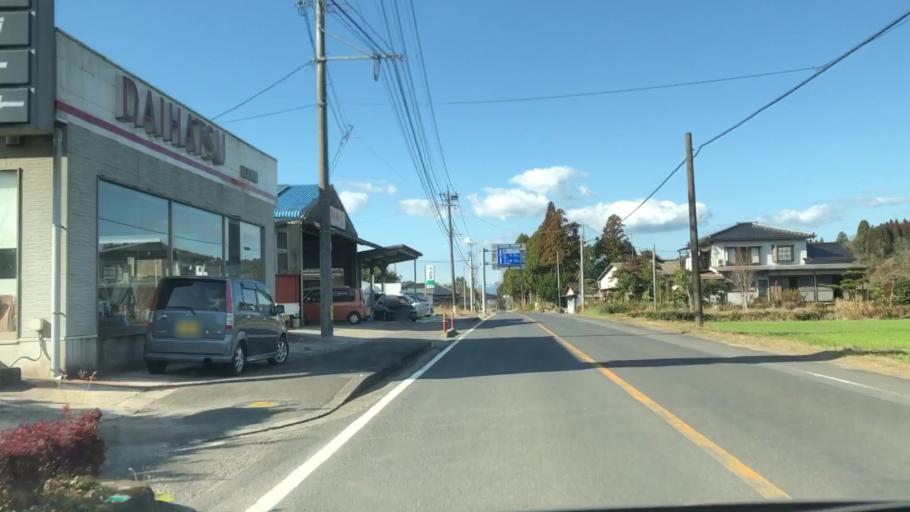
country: JP
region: Kagoshima
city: Satsumasendai
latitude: 31.7979
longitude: 130.4401
